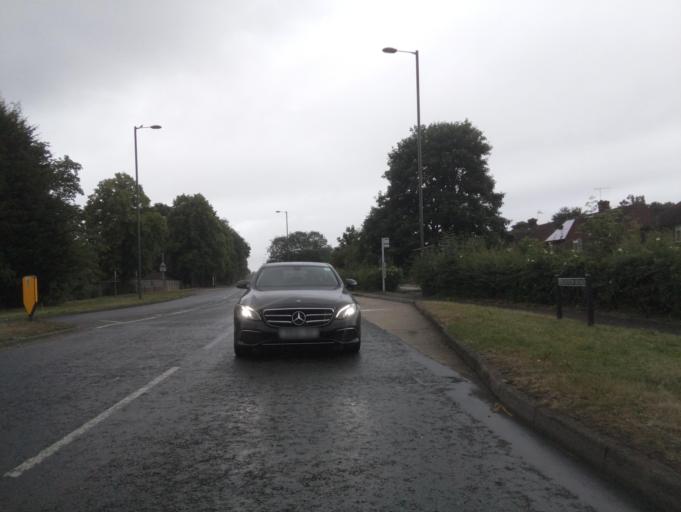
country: GB
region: England
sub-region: Surrey
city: Horley
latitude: 51.1805
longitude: -0.1644
